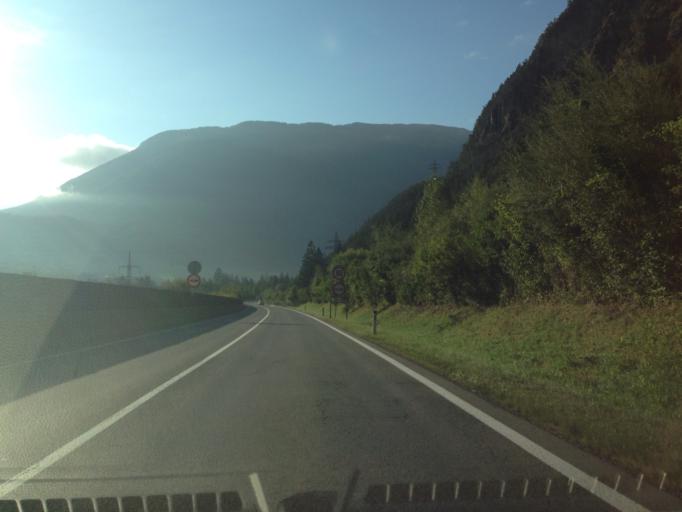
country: AT
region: Tyrol
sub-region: Politischer Bezirk Imst
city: Nassereith
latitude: 47.3139
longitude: 10.8305
